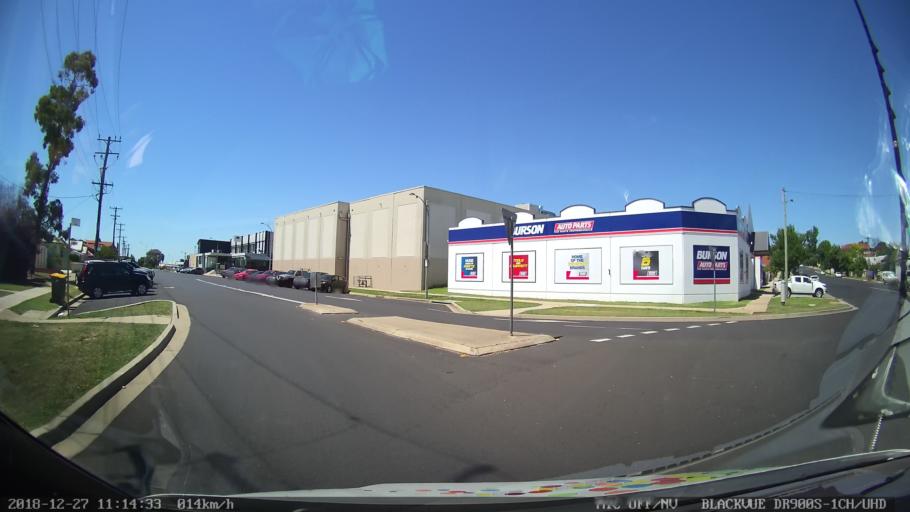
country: AU
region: New South Wales
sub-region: Bathurst Regional
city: Bathurst
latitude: -33.4198
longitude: 149.5746
